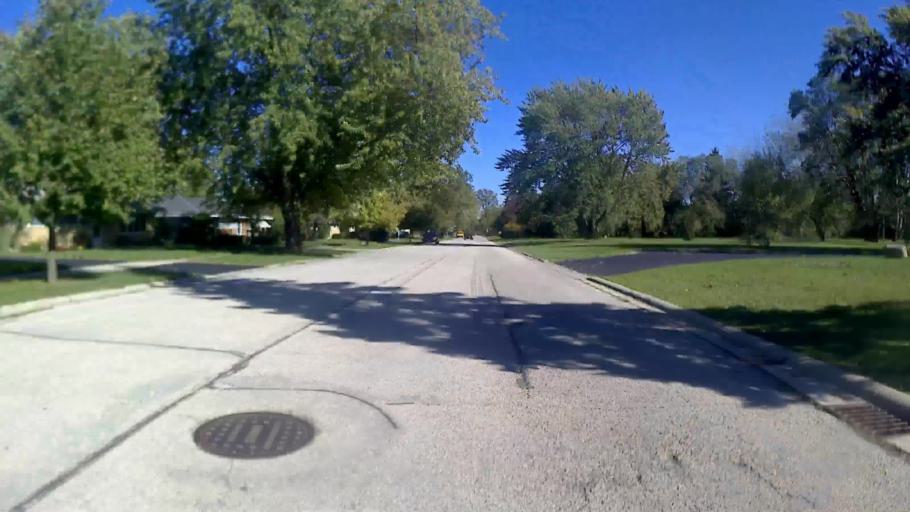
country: US
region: Illinois
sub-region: DuPage County
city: Wood Dale
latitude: 41.9545
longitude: -87.9945
